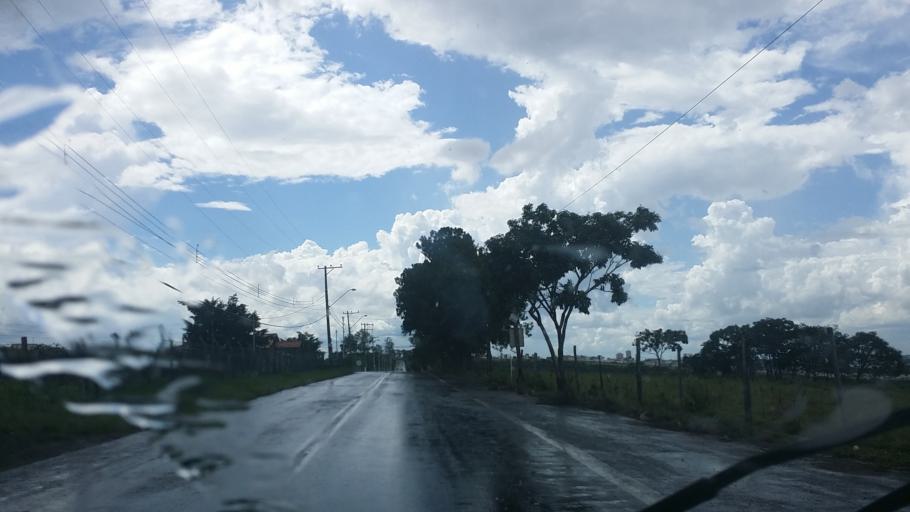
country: BR
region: Sao Paulo
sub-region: Indaiatuba
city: Indaiatuba
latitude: -23.1348
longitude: -47.1688
